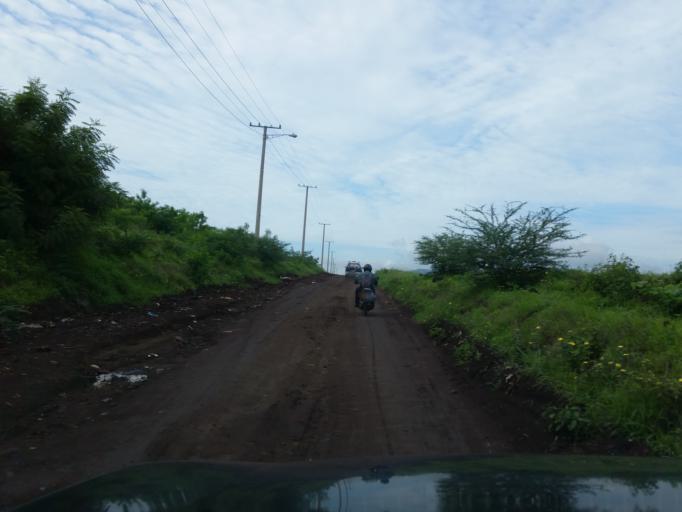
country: NI
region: Managua
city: Managua
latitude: 12.1046
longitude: -86.2050
